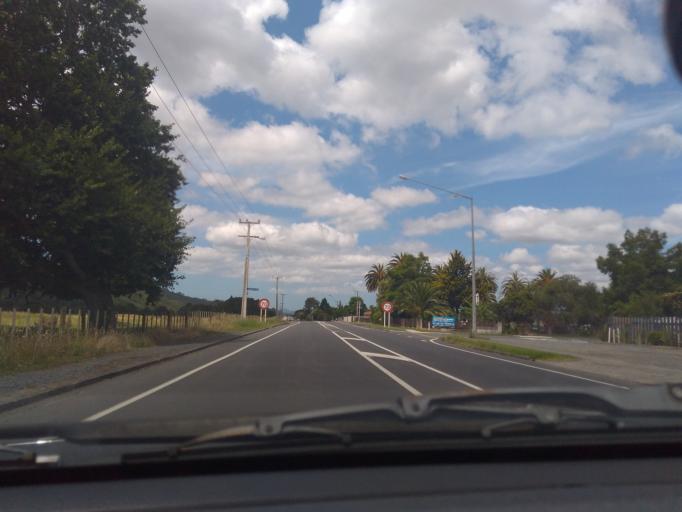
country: NZ
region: Northland
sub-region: Far North District
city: Moerewa
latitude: -35.3873
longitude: 174.0155
